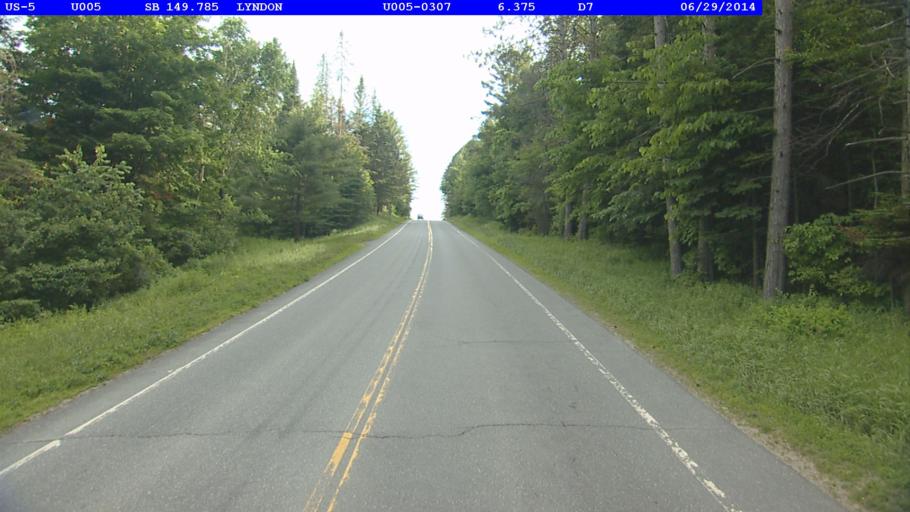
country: US
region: Vermont
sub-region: Caledonia County
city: Lyndonville
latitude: 44.5791
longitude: -71.9857
